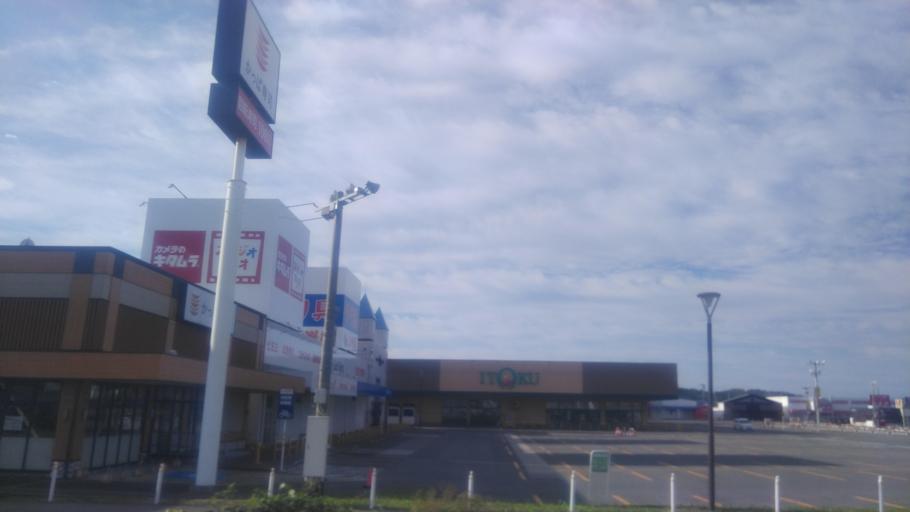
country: JP
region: Akita
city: Noshiromachi
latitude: 40.1844
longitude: 140.0539
